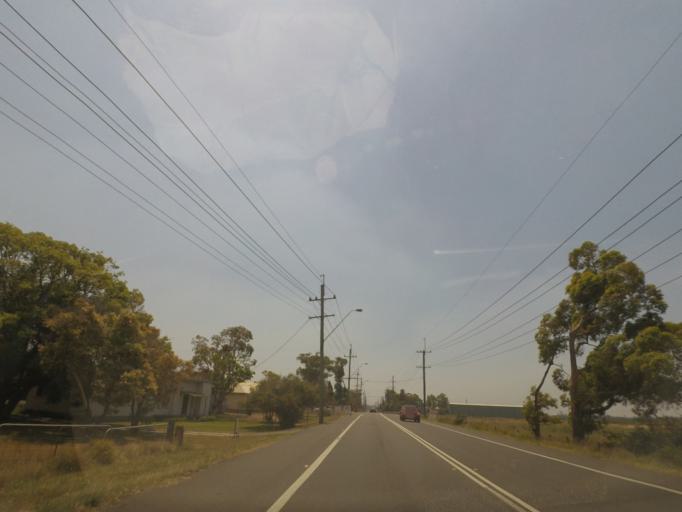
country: AU
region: New South Wales
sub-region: Newcastle
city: Mayfield West
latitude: -32.8263
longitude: 151.7385
